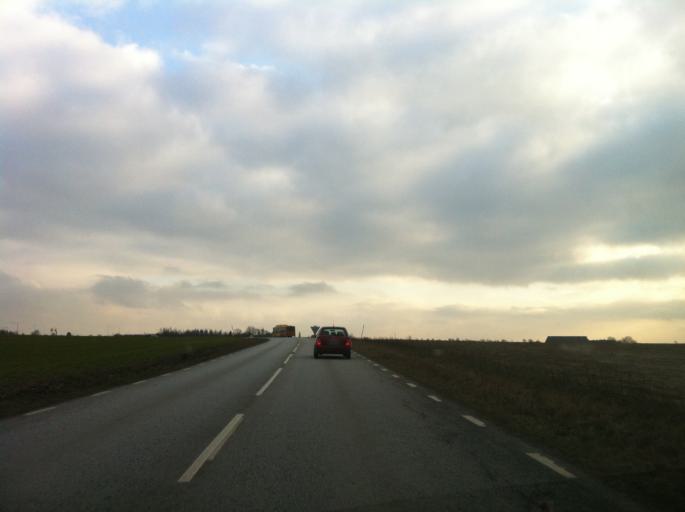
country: SE
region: Skane
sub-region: Kavlinge Kommun
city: Kaevlinge
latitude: 55.8043
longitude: 13.0927
